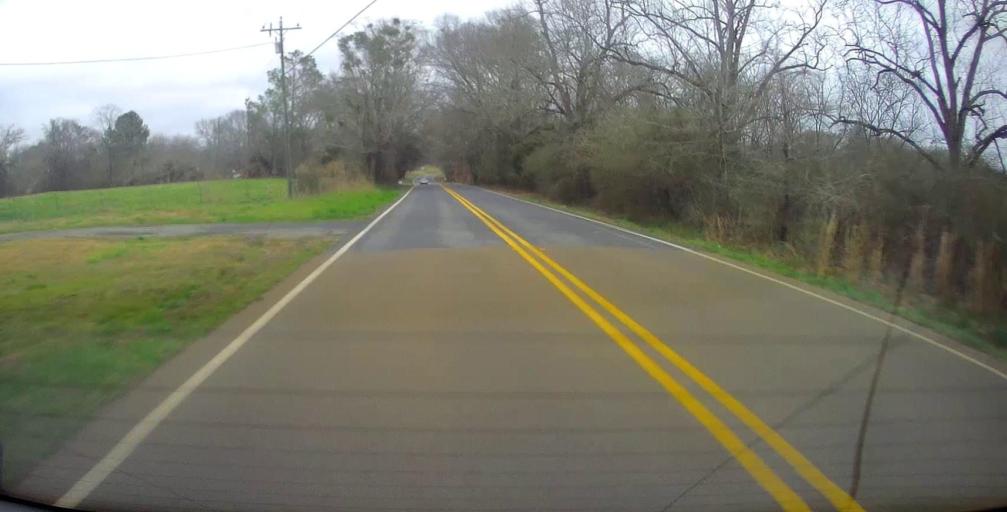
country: US
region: Georgia
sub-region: Pike County
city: Zebulon
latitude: 33.0564
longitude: -84.2900
